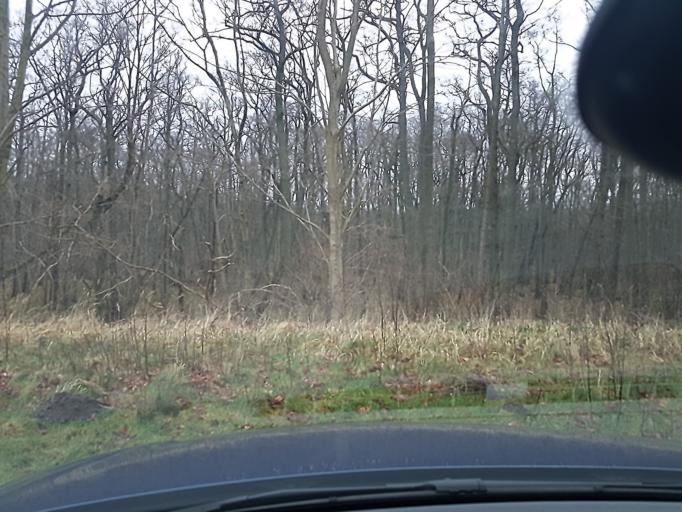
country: DE
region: Mecklenburg-Vorpommern
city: Ostseebad Binz
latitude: 54.4339
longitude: 13.5594
